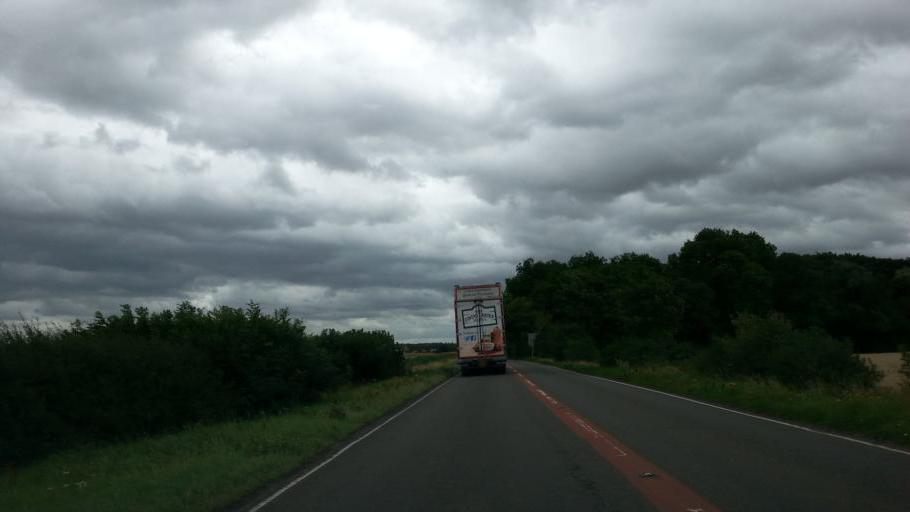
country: GB
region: England
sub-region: Cambridgeshire
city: Papworth Everard
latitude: 52.2752
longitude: -0.1371
